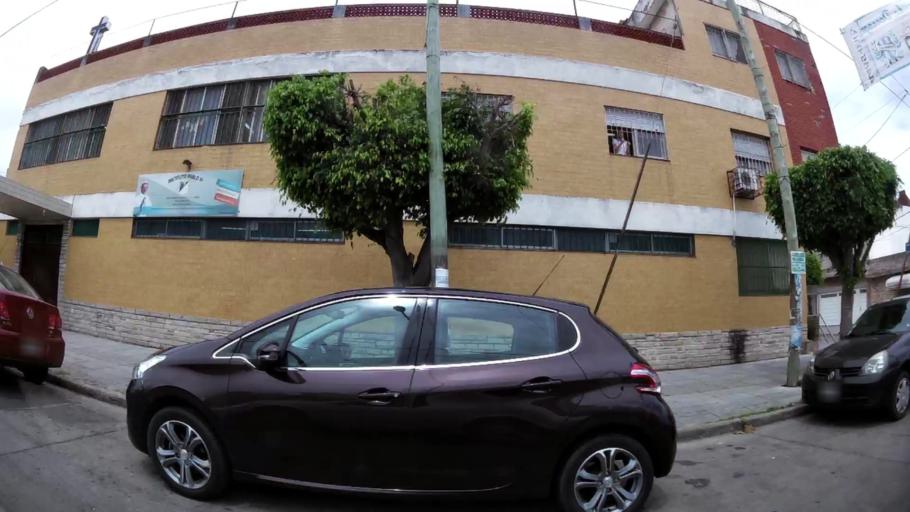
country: AR
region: Buenos Aires
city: San Justo
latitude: -34.6695
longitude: -58.5446
